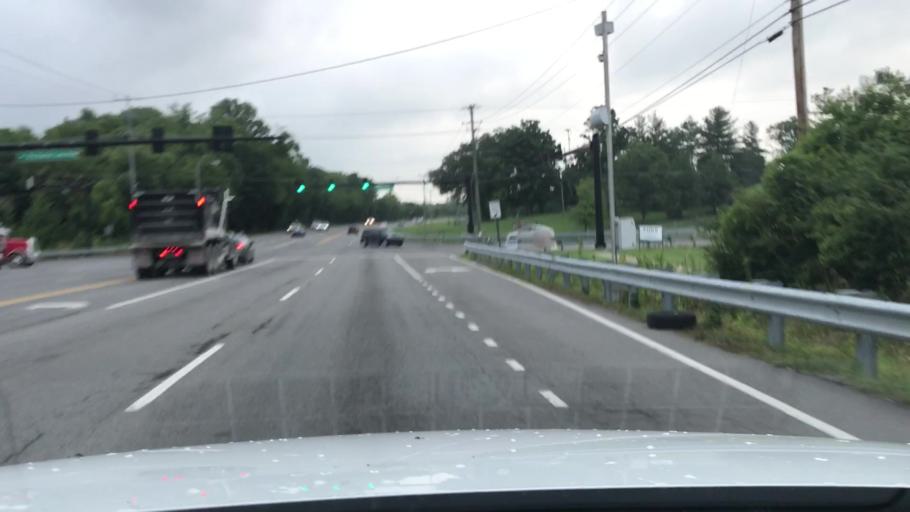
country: US
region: Tennessee
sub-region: Sumner County
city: Gallatin
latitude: 36.3458
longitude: -86.5253
